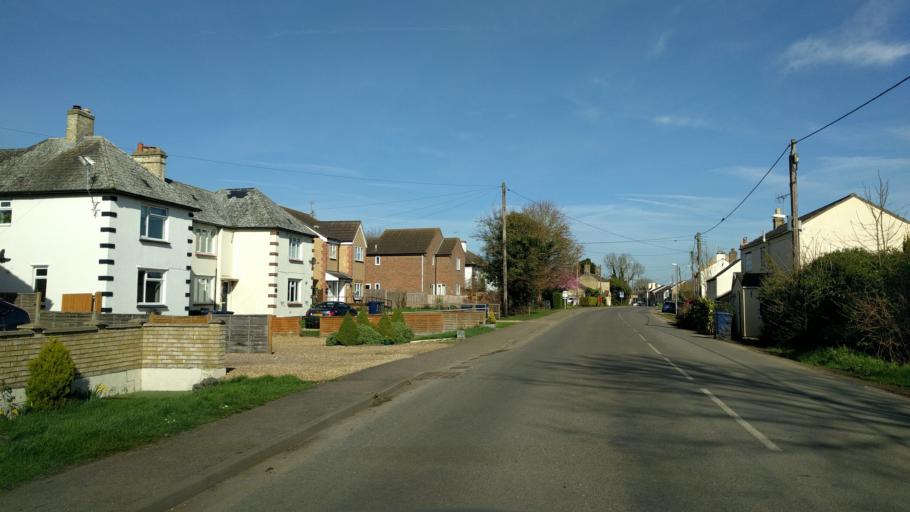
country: GB
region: England
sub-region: Cambridgeshire
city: Somersham
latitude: 52.3817
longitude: 0.0089
